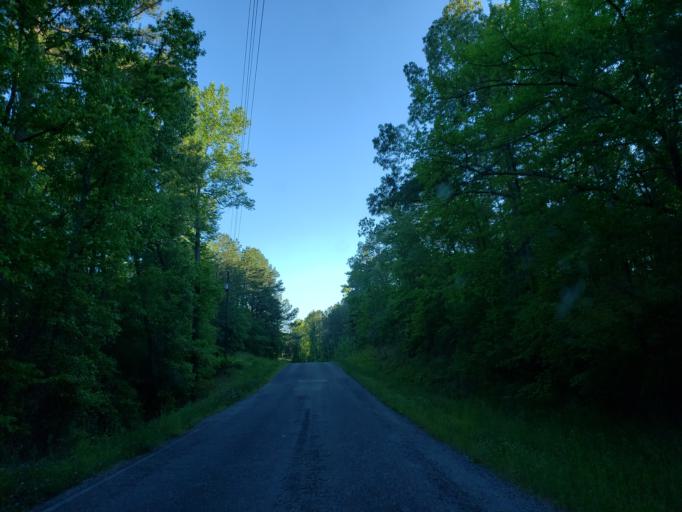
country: US
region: Georgia
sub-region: Haralson County
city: Tallapoosa
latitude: 33.7735
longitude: -85.3287
